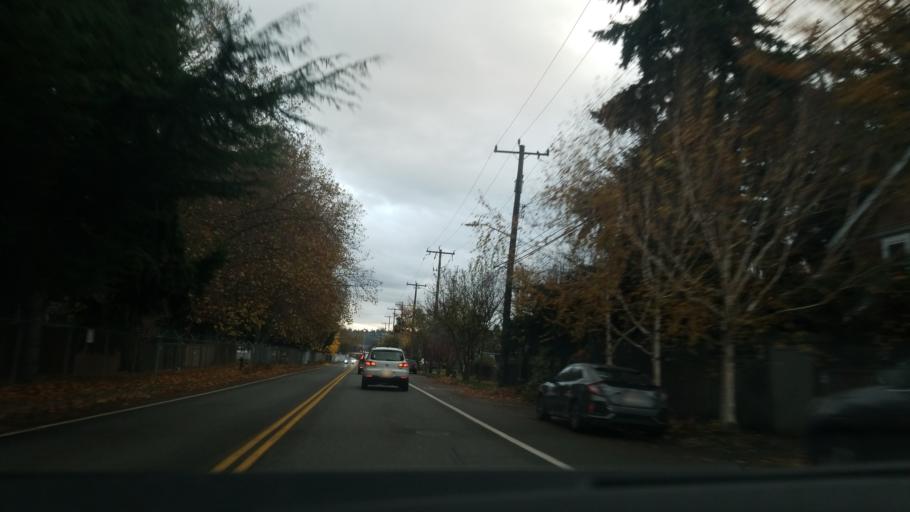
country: US
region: Washington
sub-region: King County
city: White Center
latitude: 47.5430
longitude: -122.3193
